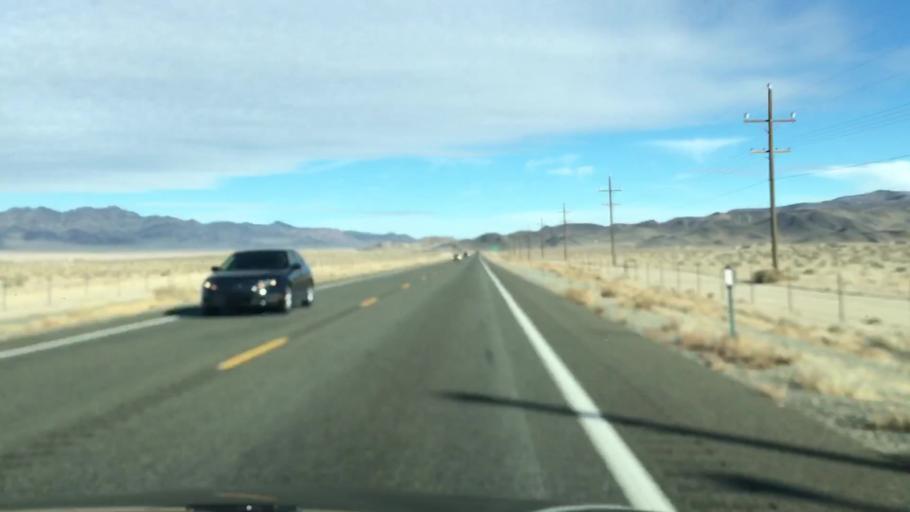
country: US
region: Nevada
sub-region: Mineral County
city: Hawthorne
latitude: 38.5275
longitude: -118.5612
